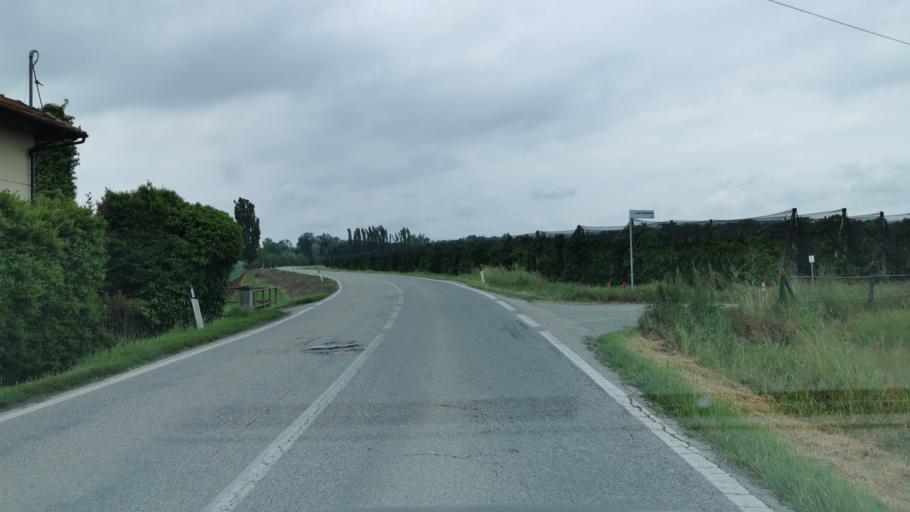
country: IT
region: Piedmont
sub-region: Provincia di Cuneo
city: Genola
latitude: 44.6150
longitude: 7.6264
